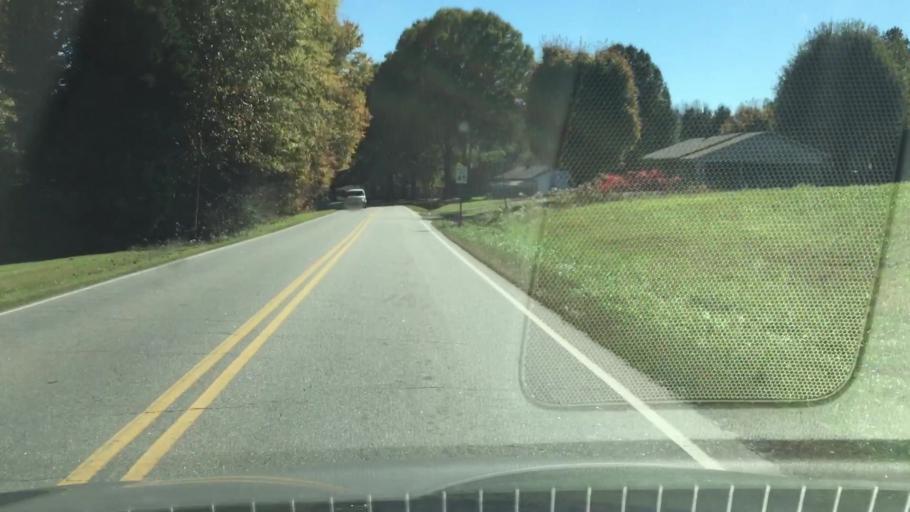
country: US
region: North Carolina
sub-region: Iredell County
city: Mooresville
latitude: 35.5414
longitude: -80.8052
